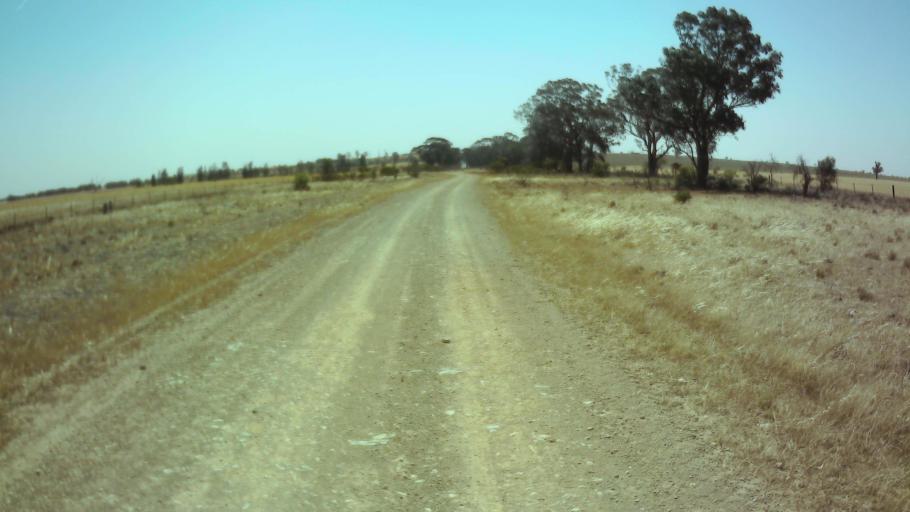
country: AU
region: New South Wales
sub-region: Weddin
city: Grenfell
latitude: -33.9135
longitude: 147.7707
